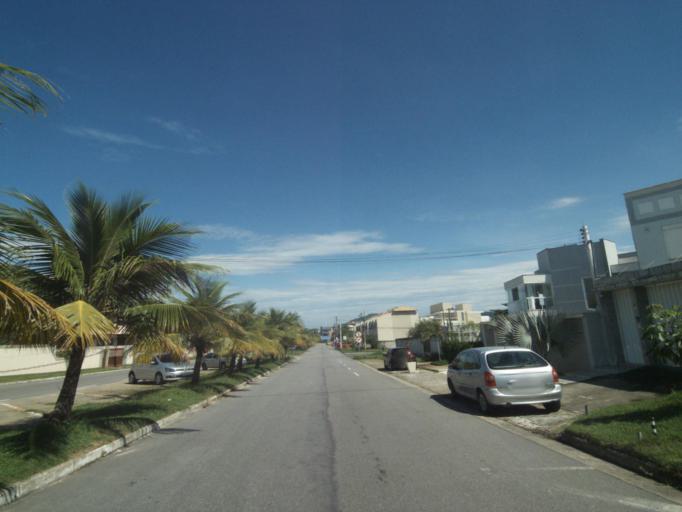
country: BR
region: Rio de Janeiro
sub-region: Niteroi
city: Niteroi
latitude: -22.9609
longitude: -43.0553
